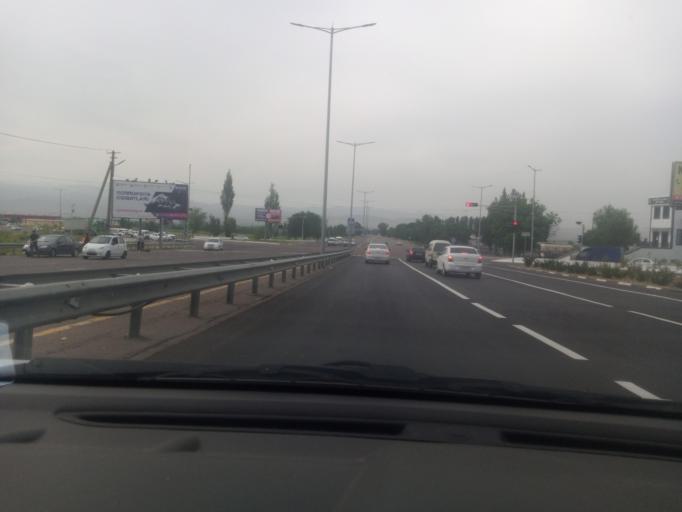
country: UZ
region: Toshkent
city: Ohangaron
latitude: 40.9212
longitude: 69.5971
